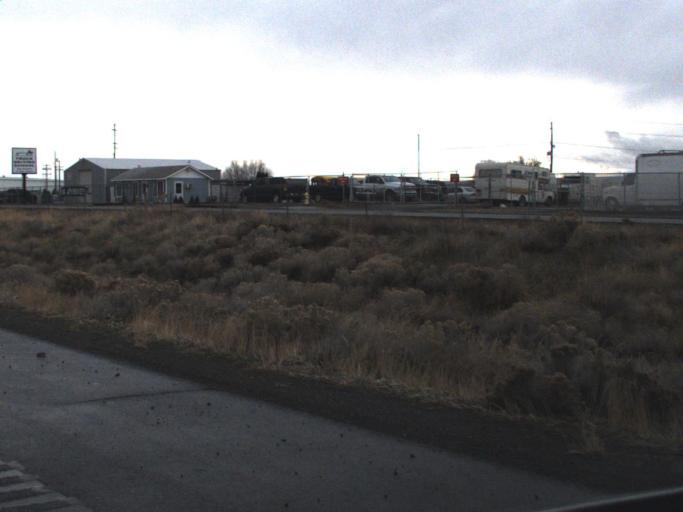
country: US
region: Washington
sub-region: Walla Walla County
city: Burbank
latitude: 46.2318
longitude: -119.0460
